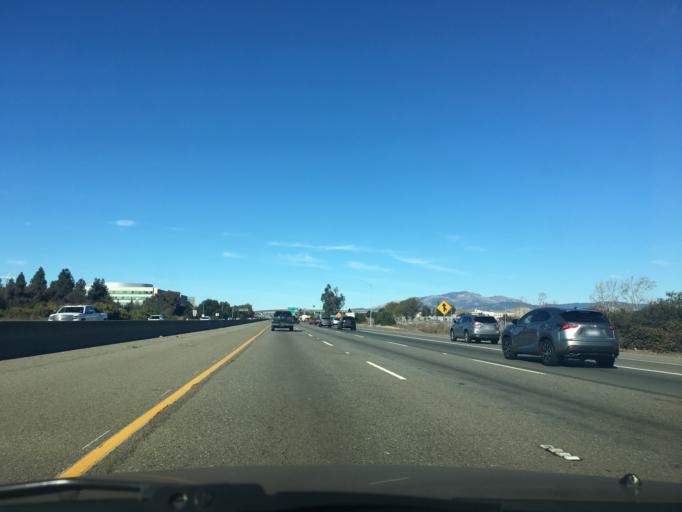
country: US
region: California
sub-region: Alameda County
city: Dublin
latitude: 37.6907
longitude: -121.9186
